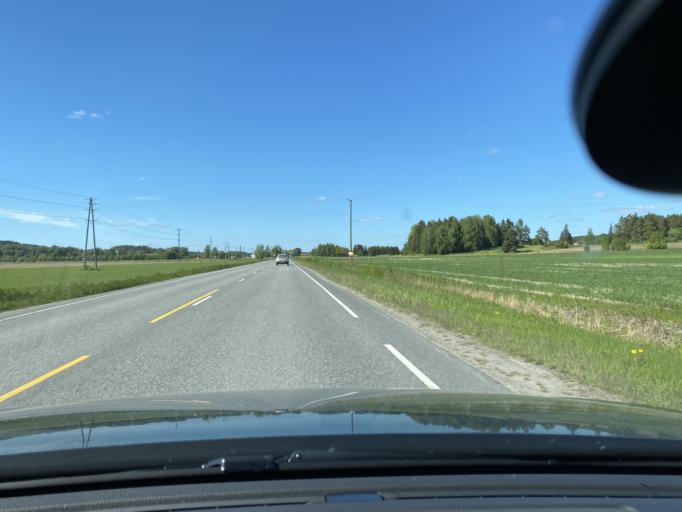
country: FI
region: Varsinais-Suomi
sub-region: Turku
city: Paimio
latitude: 60.4137
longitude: 22.6647
